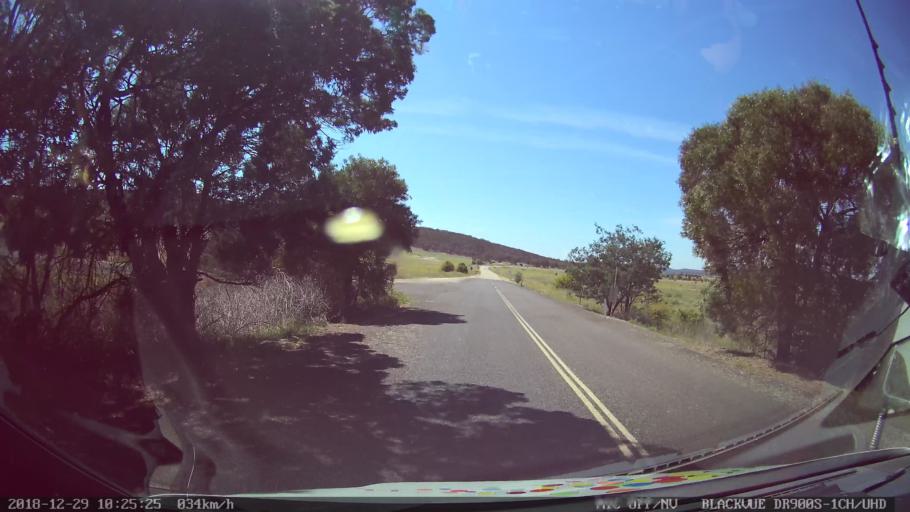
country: AU
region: New South Wales
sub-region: Yass Valley
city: Gundaroo
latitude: -34.9181
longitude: 149.4375
